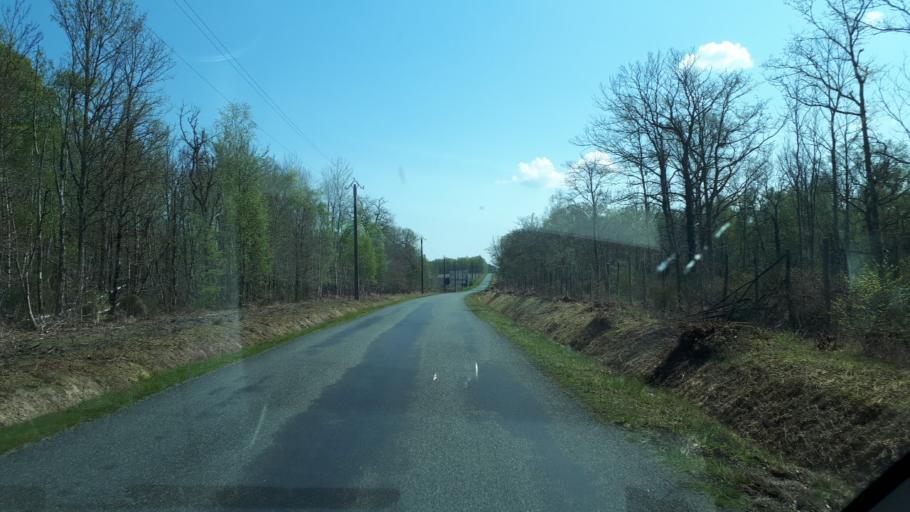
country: FR
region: Centre
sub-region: Departement du Cher
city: Neuvy-sur-Barangeon
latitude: 47.3206
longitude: 2.1872
